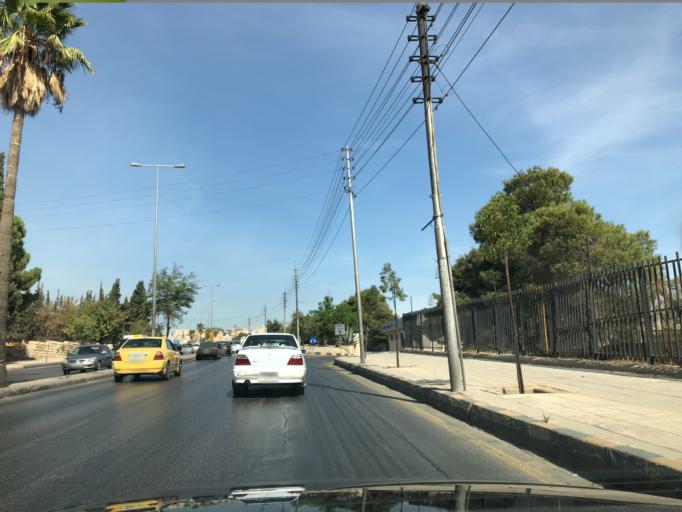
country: JO
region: Amman
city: Amman
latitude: 31.9807
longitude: 35.9023
